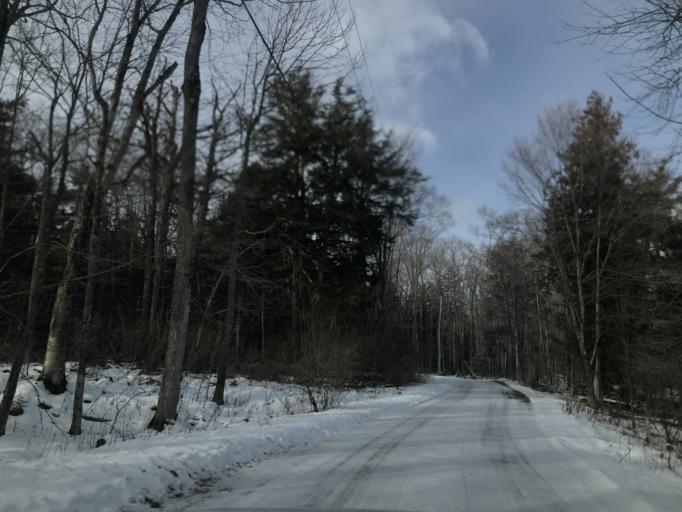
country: US
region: Wisconsin
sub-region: Door County
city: Sturgeon Bay
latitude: 45.1528
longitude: -87.0419
